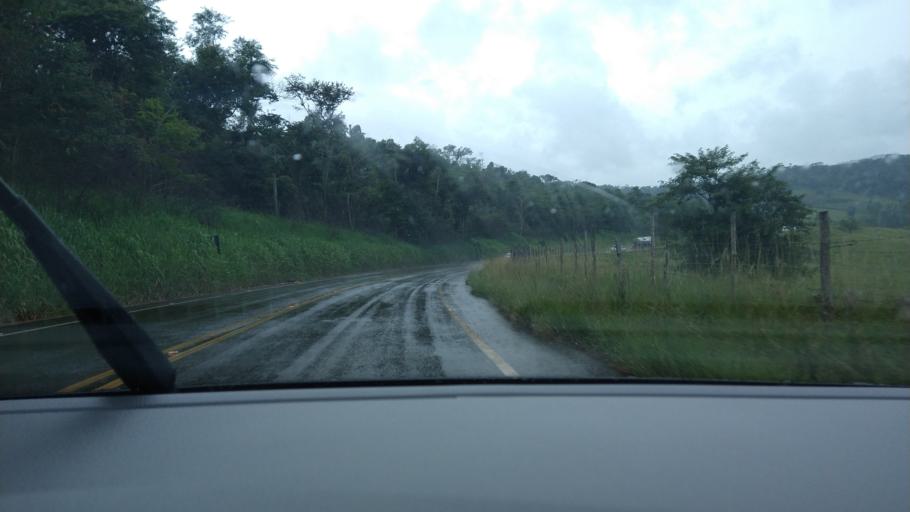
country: BR
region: Minas Gerais
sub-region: Vicosa
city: Vicosa
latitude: -20.6093
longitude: -42.8683
